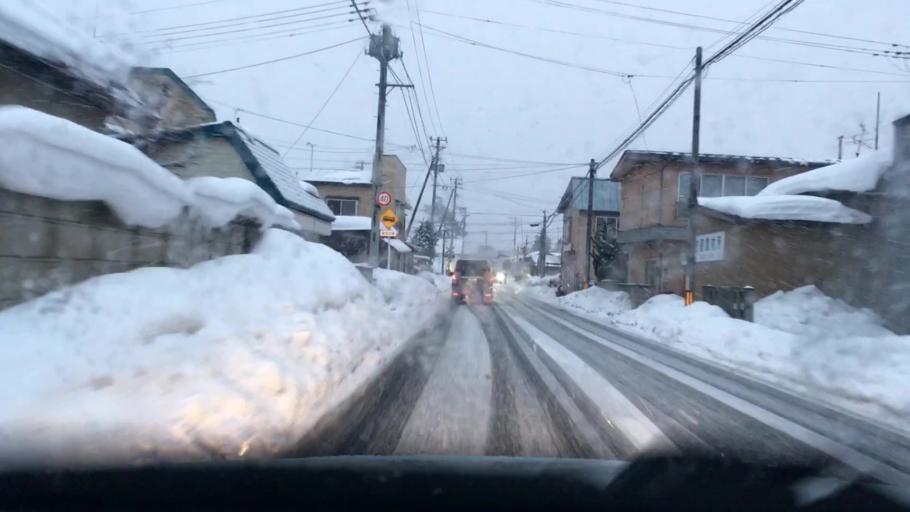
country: JP
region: Aomori
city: Hirosaki
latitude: 40.5638
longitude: 140.4863
